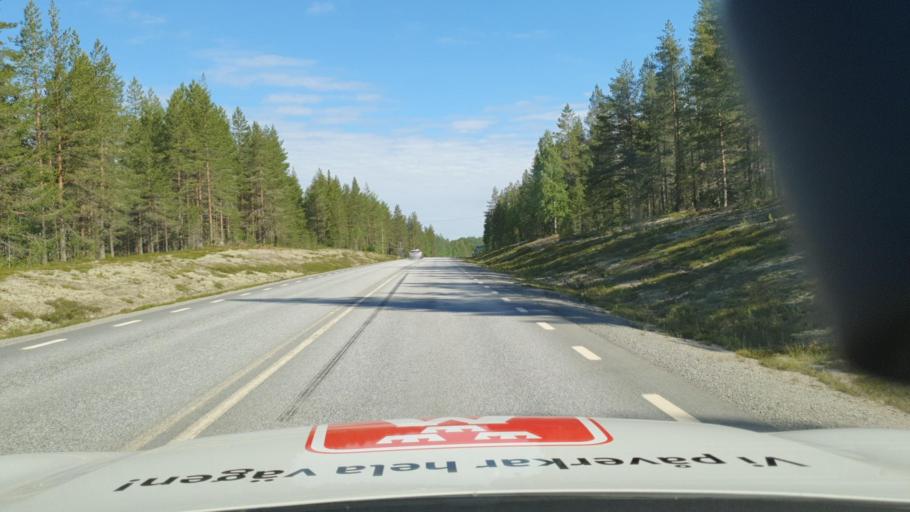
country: SE
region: Vaesterbotten
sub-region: Vannas Kommun
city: Vannasby
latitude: 64.0629
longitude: 19.9927
